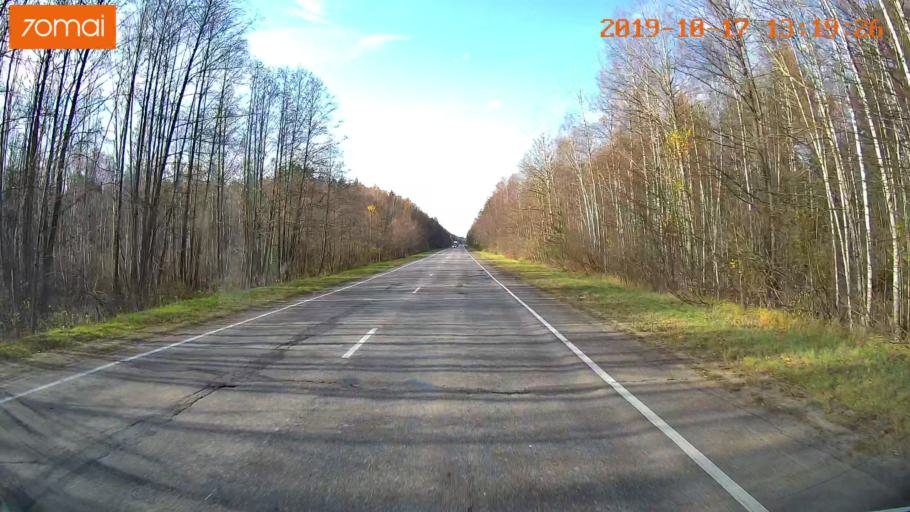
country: RU
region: Rjazan
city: Gus'-Zheleznyy
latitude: 55.0693
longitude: 41.0743
